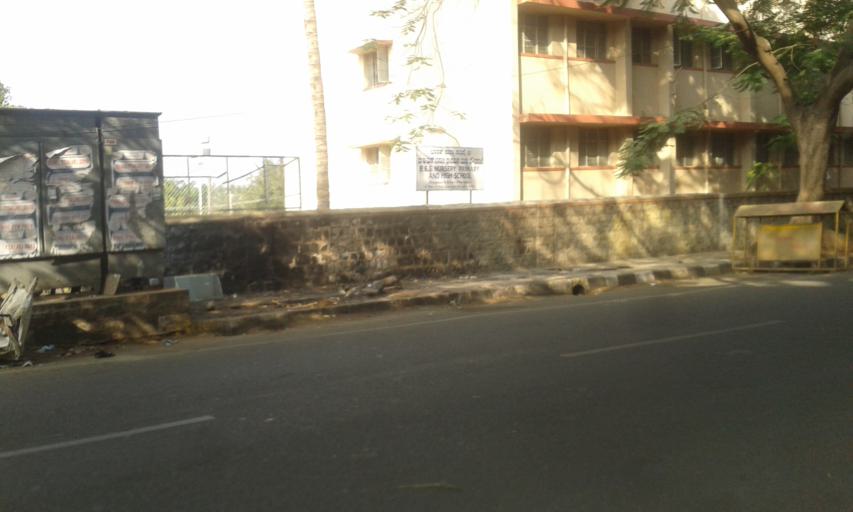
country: IN
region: Karnataka
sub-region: Bangalore Urban
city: Bangalore
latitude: 12.9262
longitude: 77.5890
